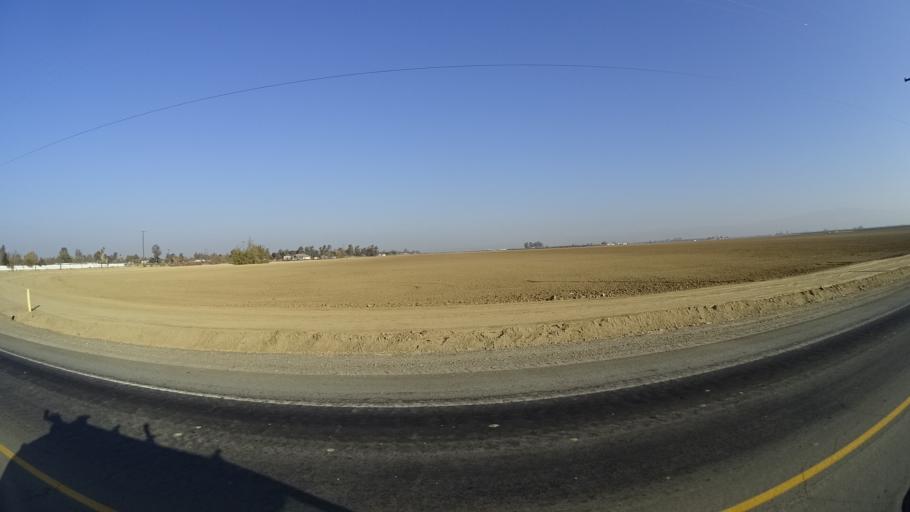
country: US
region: California
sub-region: Kern County
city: Weedpatch
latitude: 35.2377
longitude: -118.9596
